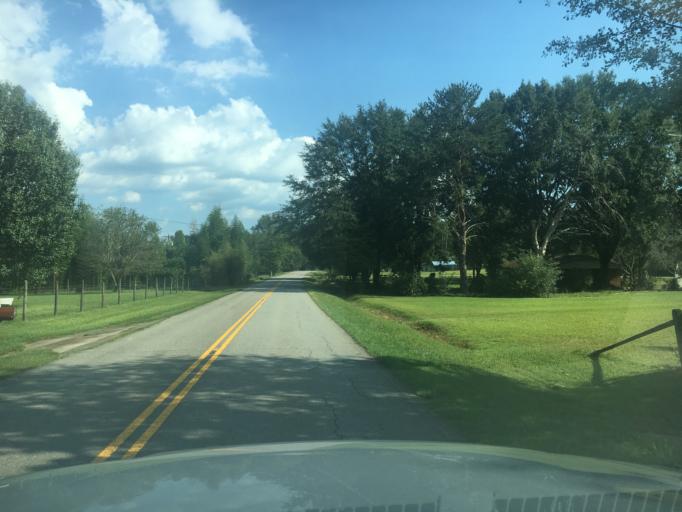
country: US
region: South Carolina
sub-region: Pickens County
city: Liberty
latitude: 34.7425
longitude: -82.6507
